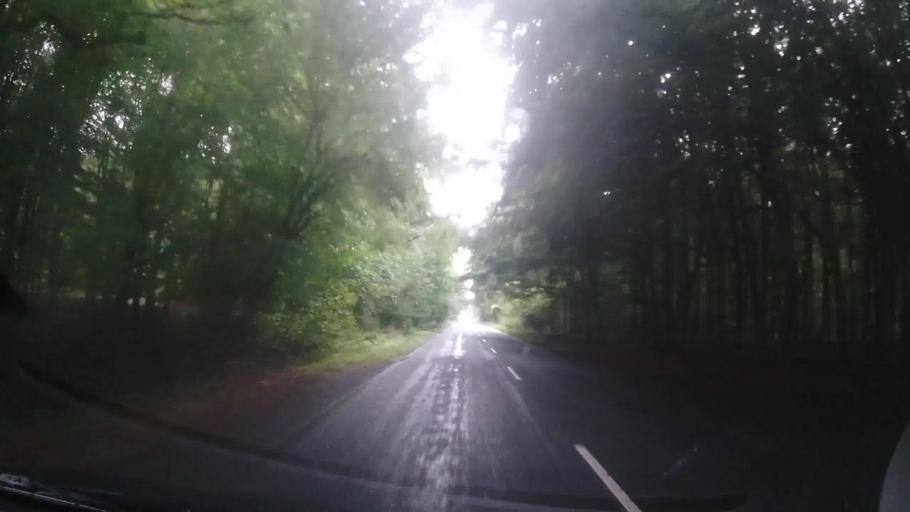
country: GB
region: England
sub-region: Oxfordshire
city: Stonesfield
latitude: 51.8712
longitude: -1.4273
